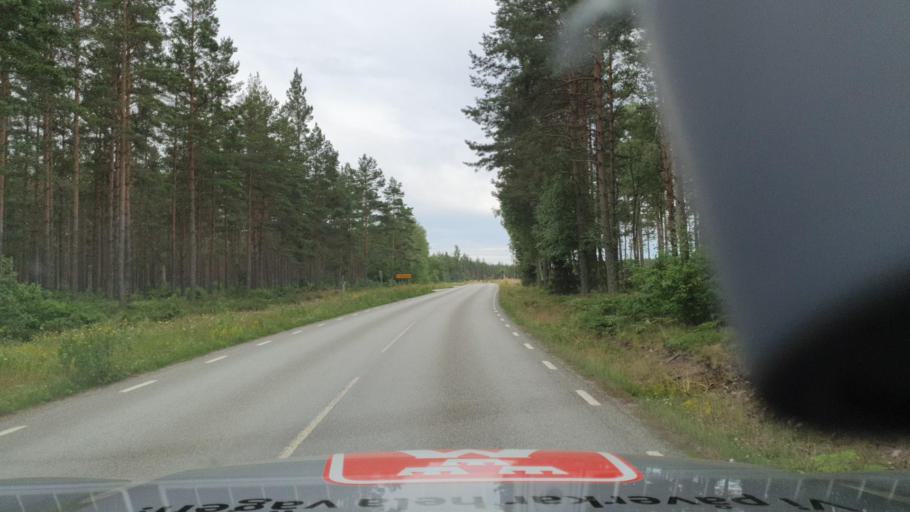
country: SE
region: Kalmar
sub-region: Kalmar Kommun
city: Trekanten
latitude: 56.6310
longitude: 16.0328
